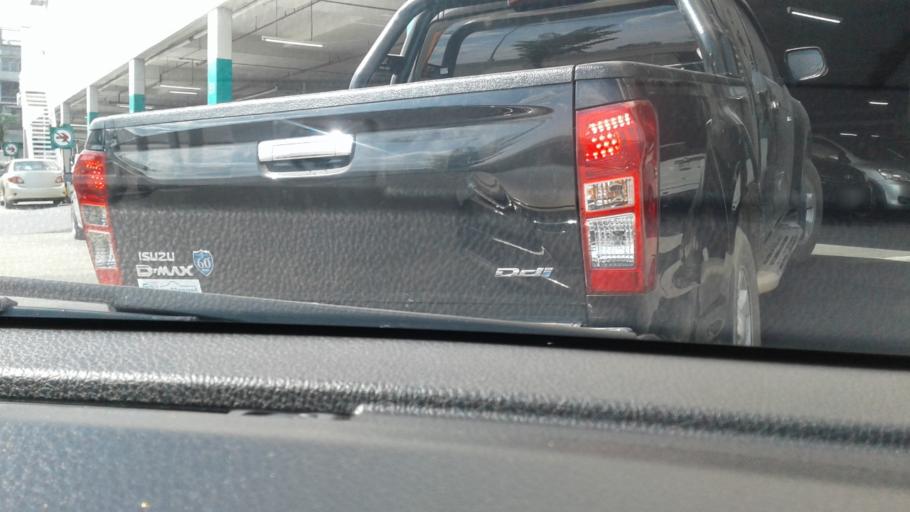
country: TH
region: Phra Nakhon Si Ayutthaya
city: Ban Bang Kadi Pathum Thani
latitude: 13.9932
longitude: 100.6128
